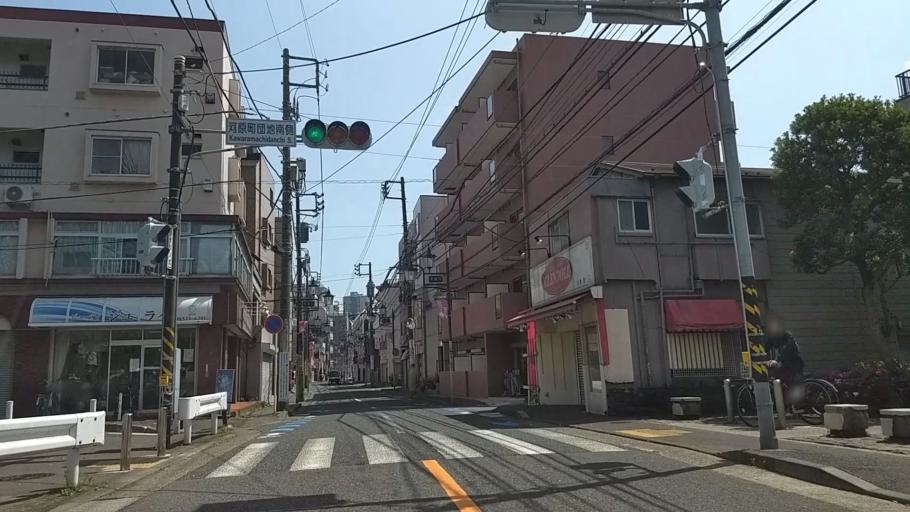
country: JP
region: Kanagawa
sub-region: Kawasaki-shi
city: Kawasaki
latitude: 35.5384
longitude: 139.6916
